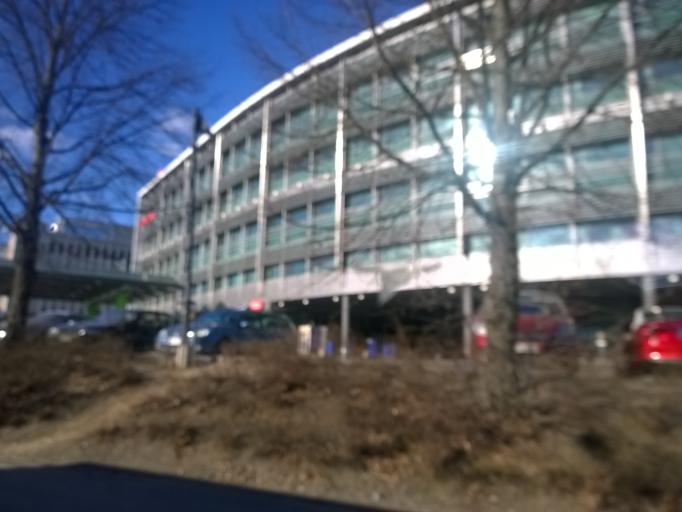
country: FI
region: Pirkanmaa
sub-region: Tampere
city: Tampere
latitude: 61.4919
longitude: 23.7719
